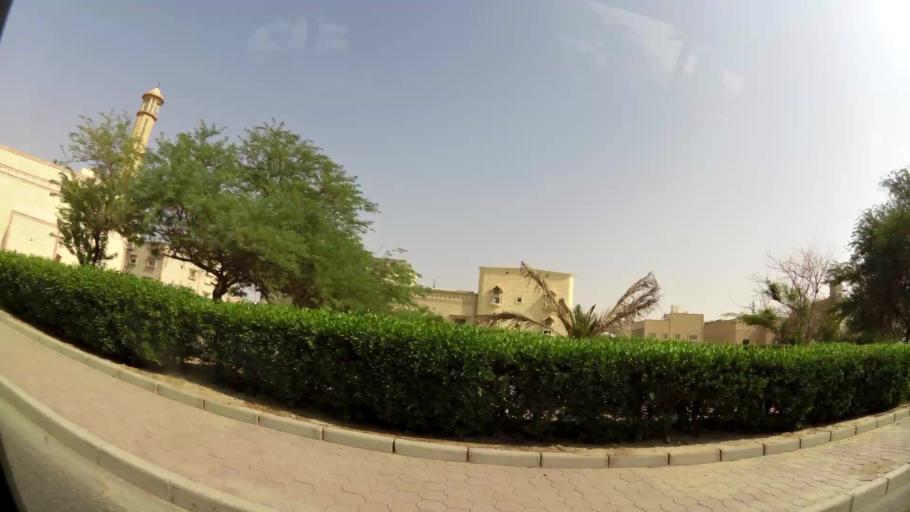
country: KW
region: Muhafazat al Jahra'
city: Al Jahra'
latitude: 29.3292
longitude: 47.6474
